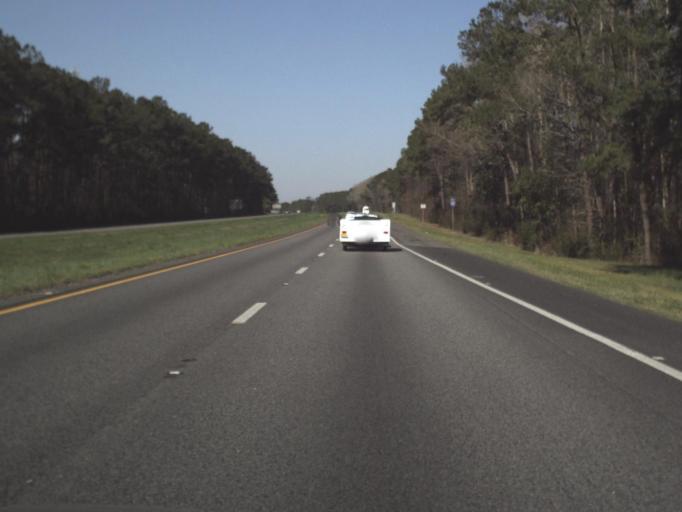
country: US
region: Florida
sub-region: Jefferson County
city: Monticello
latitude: 30.4772
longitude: -83.8976
